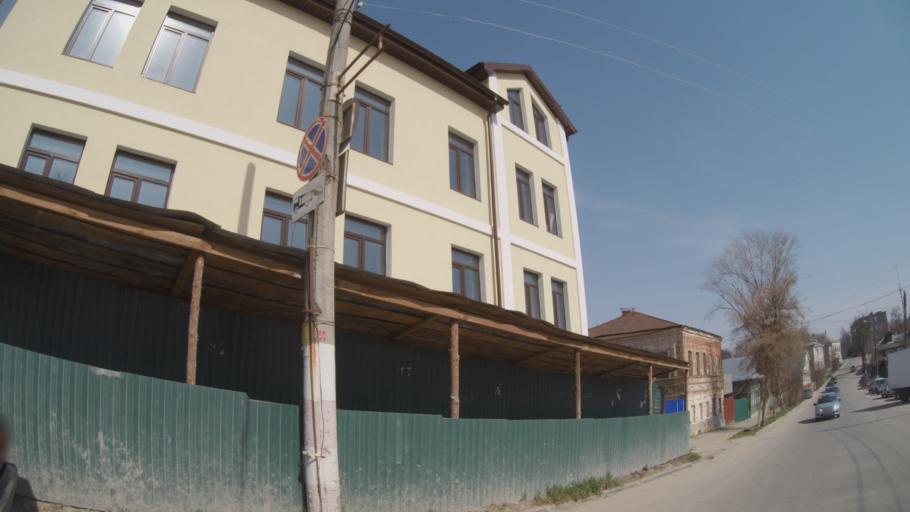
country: RU
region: Nizjnij Novgorod
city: Arzamas
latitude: 55.3875
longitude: 43.8169
